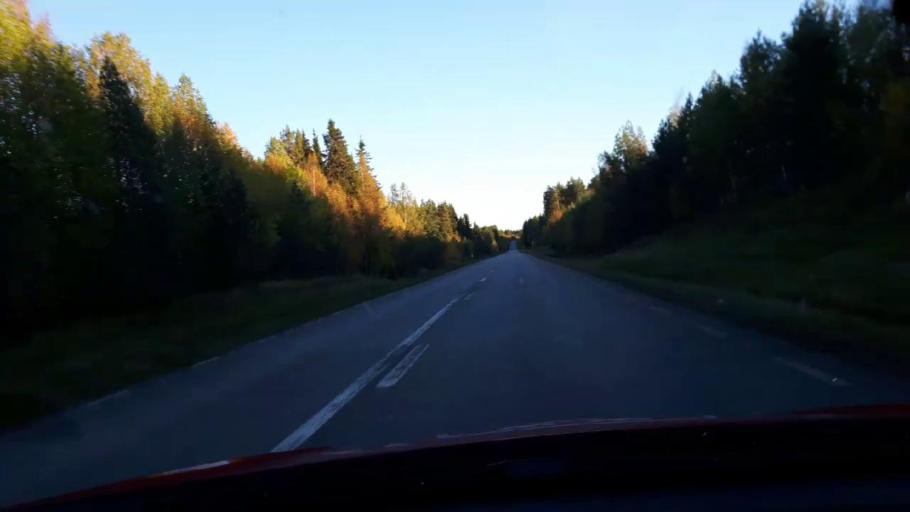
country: SE
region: Jaemtland
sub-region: Krokoms Kommun
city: Krokom
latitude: 63.4470
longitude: 14.4920
